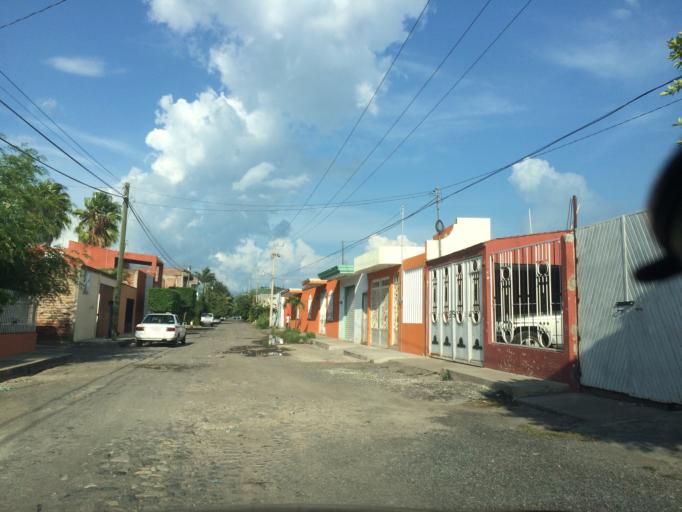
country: MX
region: Nayarit
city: Ixtlan del Rio
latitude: 21.0360
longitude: -104.3866
